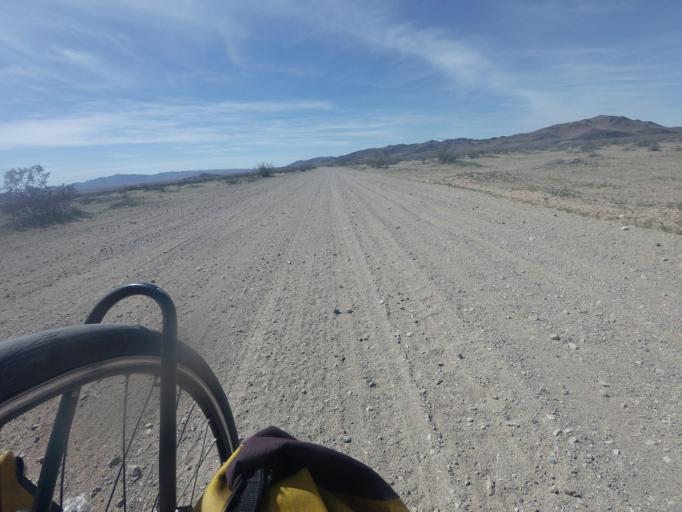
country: US
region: California
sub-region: San Bernardino County
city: Searles Valley
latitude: 35.5988
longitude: -117.3961
